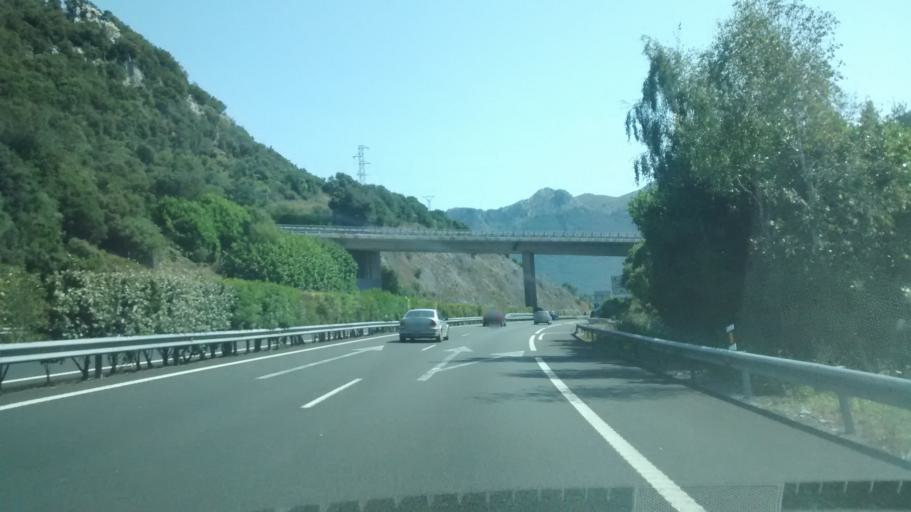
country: ES
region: Cantabria
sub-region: Provincia de Cantabria
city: Liendo
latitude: 43.3908
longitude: -3.3387
